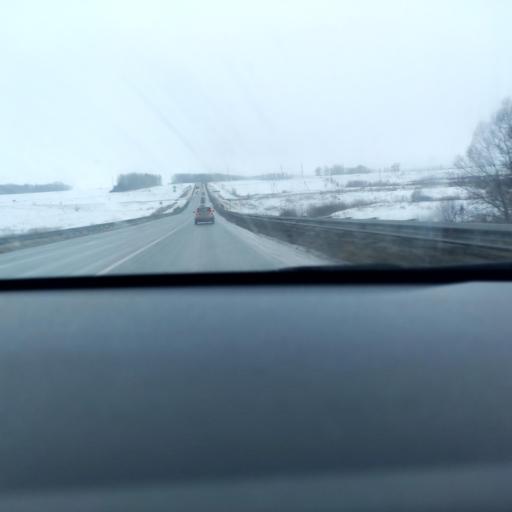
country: RU
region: Tatarstan
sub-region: Chistopol'skiy Rayon
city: Chistopol'
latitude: 55.3174
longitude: 50.4160
